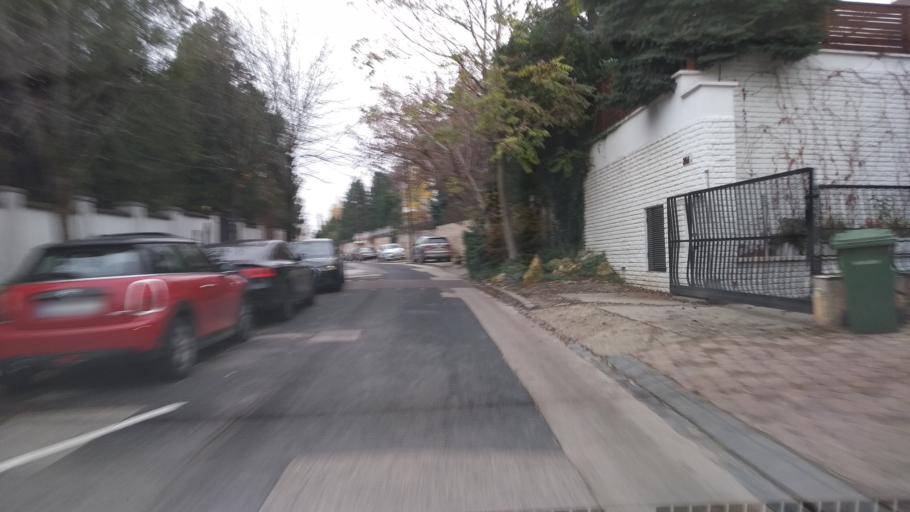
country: HU
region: Budapest
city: Budapest II. keruelet
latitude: 47.5217
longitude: 19.0105
